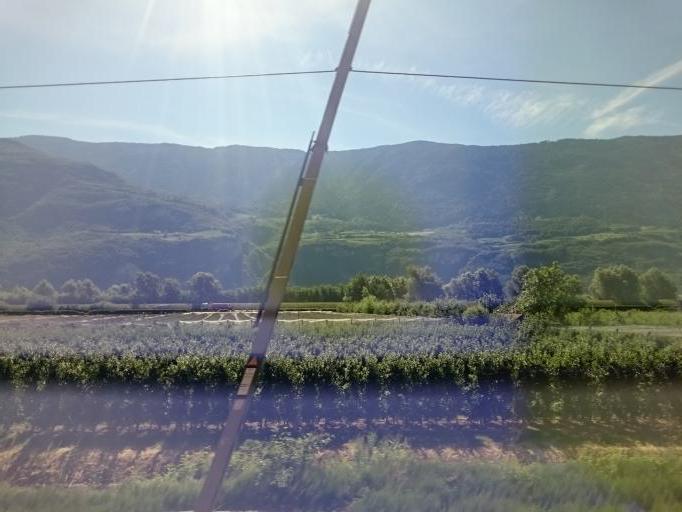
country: IT
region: Trentino-Alto Adige
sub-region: Bolzano
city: Cortina sulla Strada del Vino
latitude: 46.2628
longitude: 11.2243
